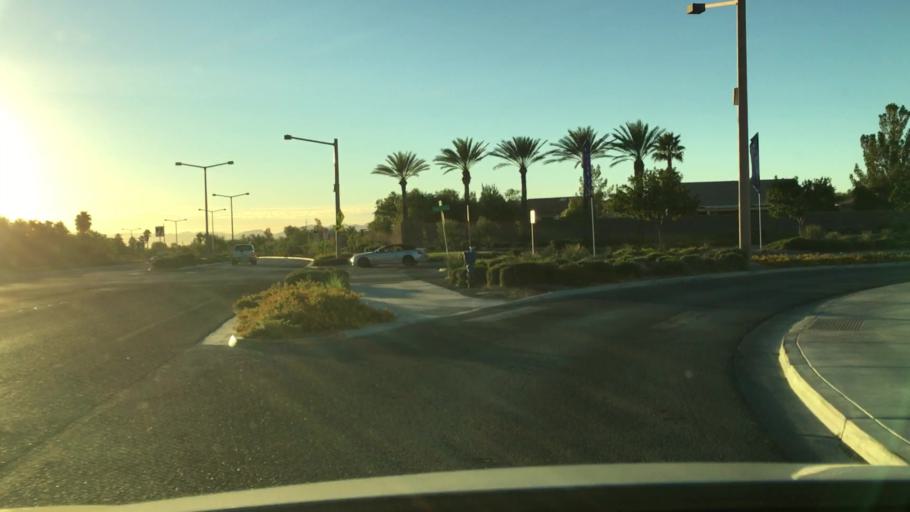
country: US
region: Nevada
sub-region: Clark County
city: Summerlin South
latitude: 36.1001
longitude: -115.3249
